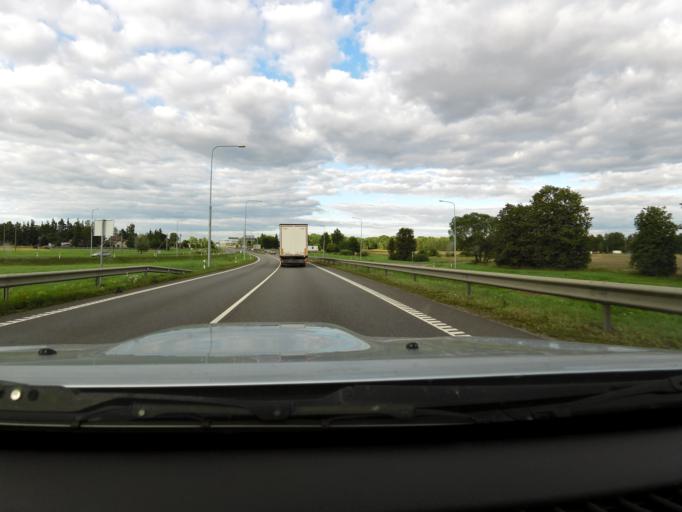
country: LT
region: Marijampoles apskritis
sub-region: Marijampole Municipality
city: Marijampole
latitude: 54.5851
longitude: 23.3808
